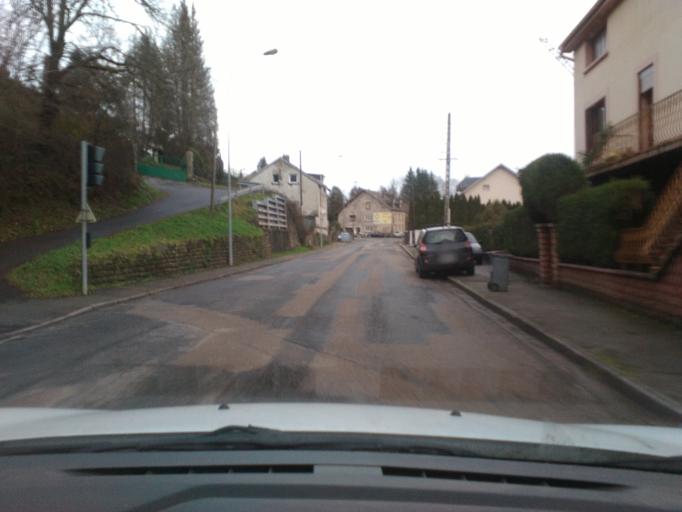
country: FR
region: Lorraine
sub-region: Departement des Vosges
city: Senones
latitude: 48.3946
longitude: 6.9718
